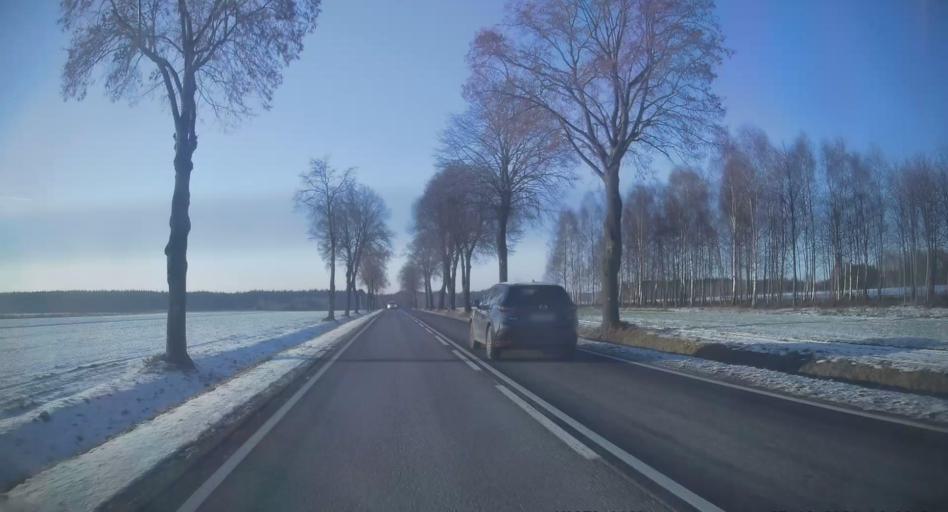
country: PL
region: Lodz Voivodeship
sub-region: Powiat opoczynski
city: Mniszkow
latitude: 51.3329
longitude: 20.0185
